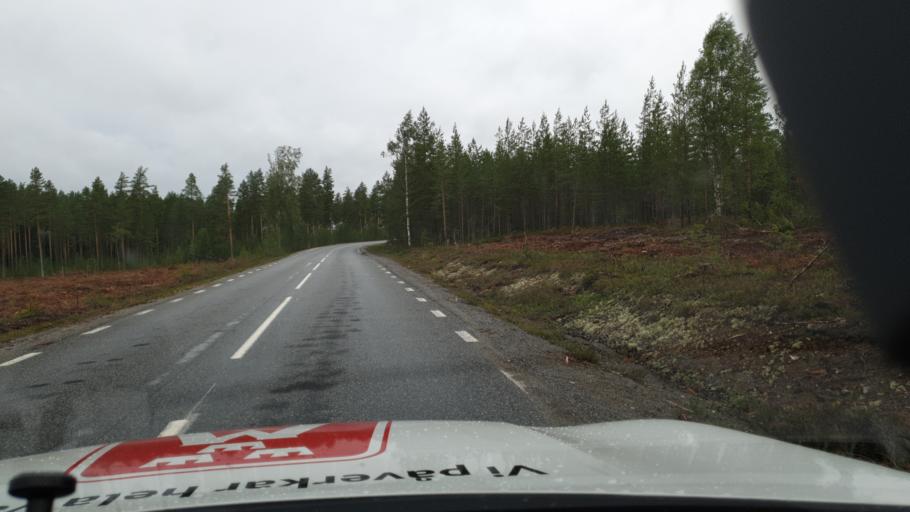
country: SE
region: Vaesterbotten
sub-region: Umea Kommun
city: Saevar
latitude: 63.9655
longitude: 20.5079
